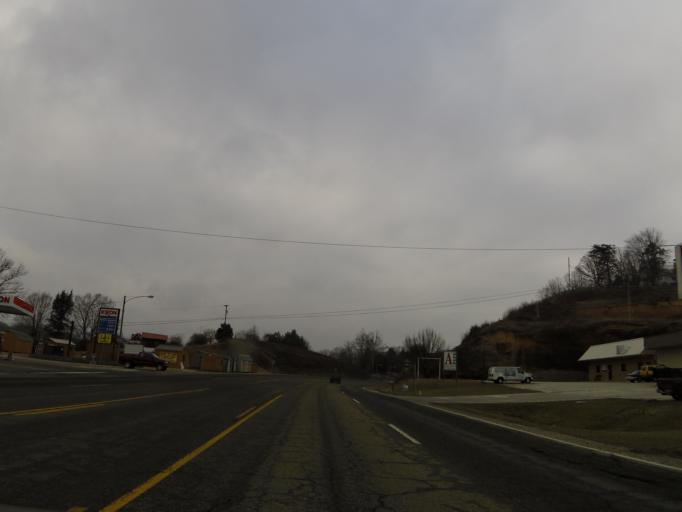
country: US
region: Tennessee
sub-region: Morgan County
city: Wartburg
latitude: 36.1060
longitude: -84.5944
